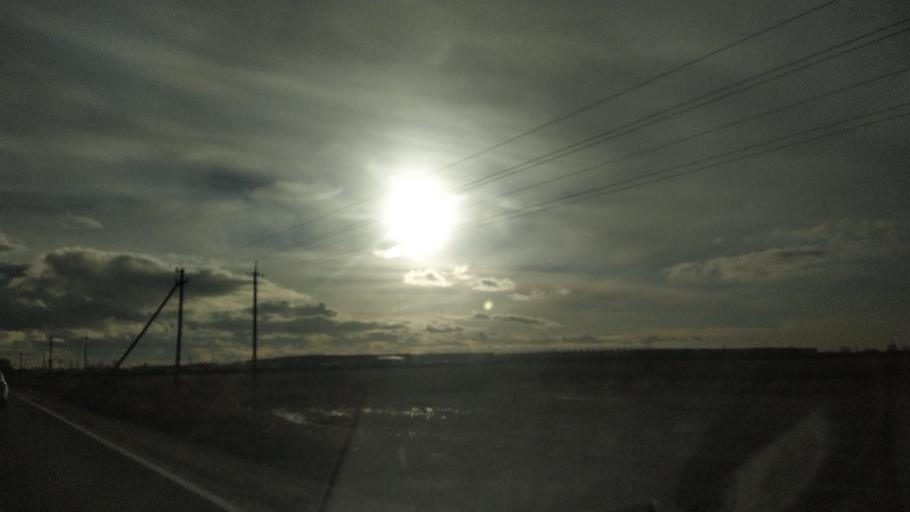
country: RU
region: St.-Petersburg
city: Petro-Slavyanka
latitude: 59.7772
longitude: 30.4808
